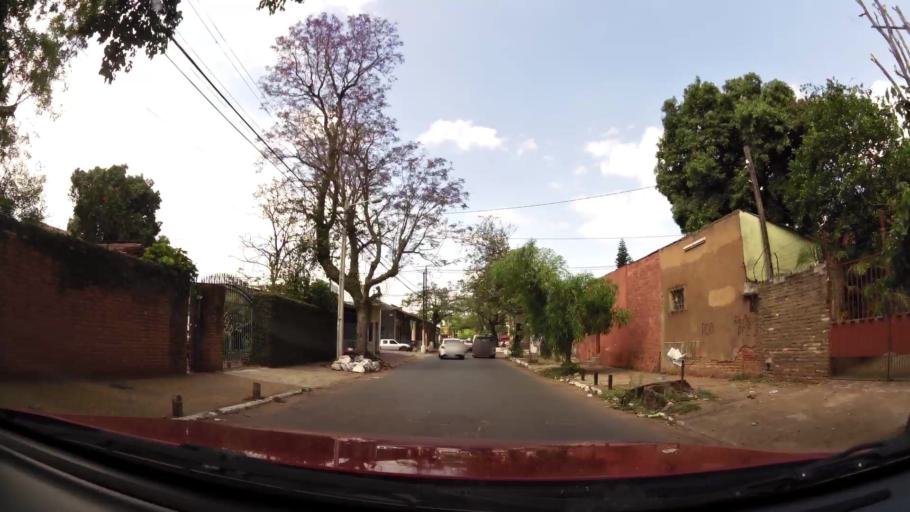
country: PY
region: Central
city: San Lorenzo
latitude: -25.3401
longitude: -57.5093
